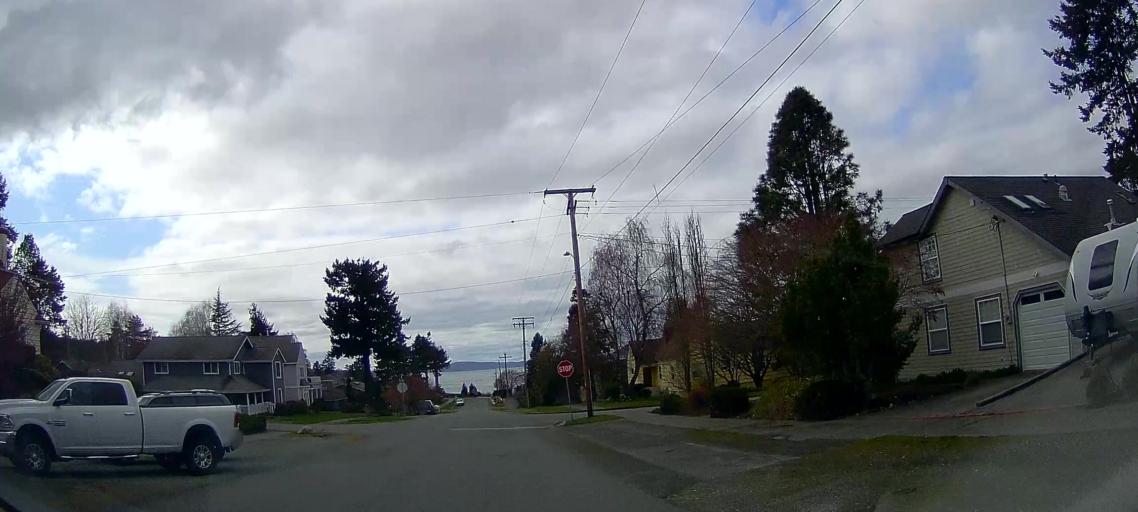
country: US
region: Washington
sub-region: Skagit County
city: Anacortes
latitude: 48.5144
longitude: -122.6294
